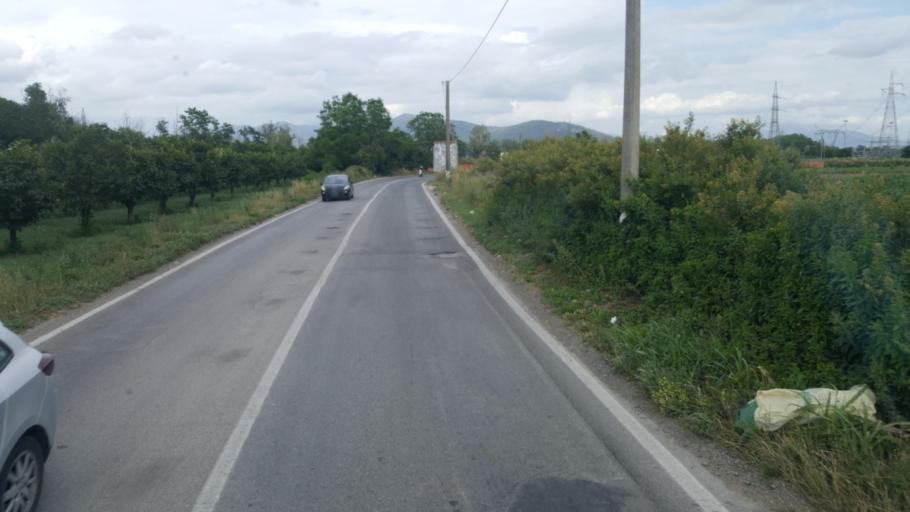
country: IT
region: Campania
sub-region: Provincia di Caserta
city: Maddaloni
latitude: 41.0119
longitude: 14.3775
